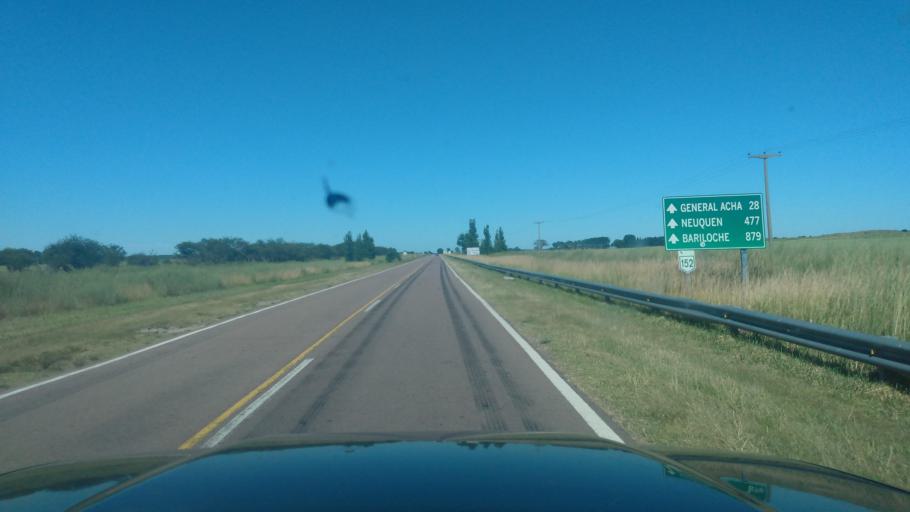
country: AR
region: La Pampa
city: General Acha
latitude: -37.3136
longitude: -64.2957
